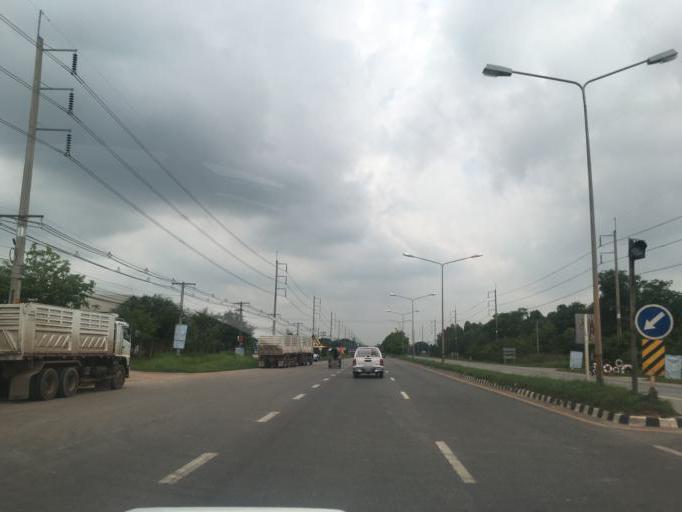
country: TH
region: Changwat Udon Thani
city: Udon Thani
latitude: 17.3763
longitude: 102.7355
